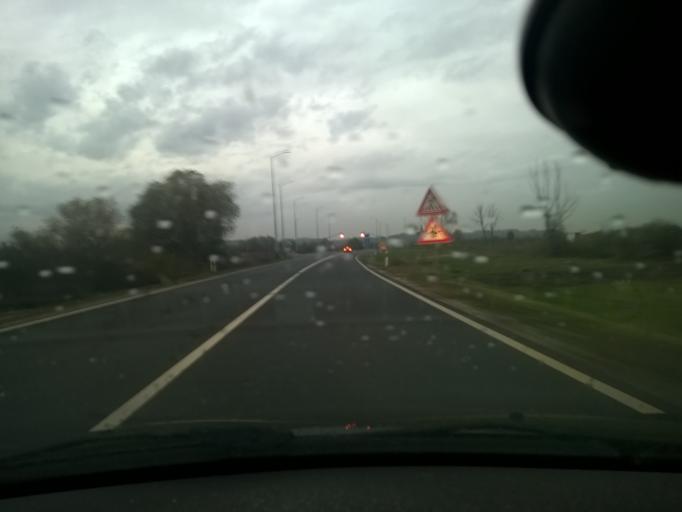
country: HR
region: Zagrebacka
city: Pojatno
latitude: 45.9324
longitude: 15.8196
